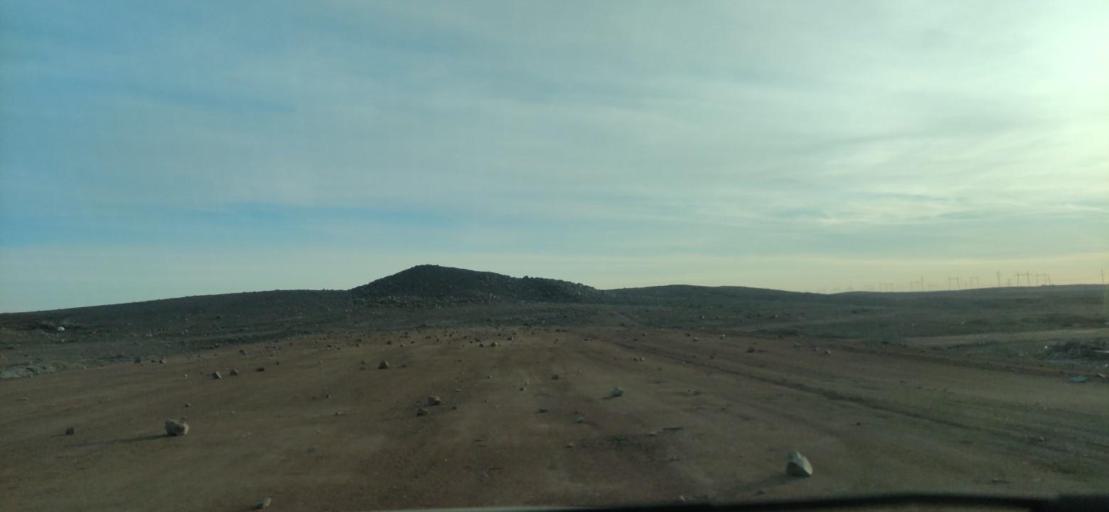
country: KZ
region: Qaraghandy
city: Saryshaghan
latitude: 46.1176
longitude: 73.5947
